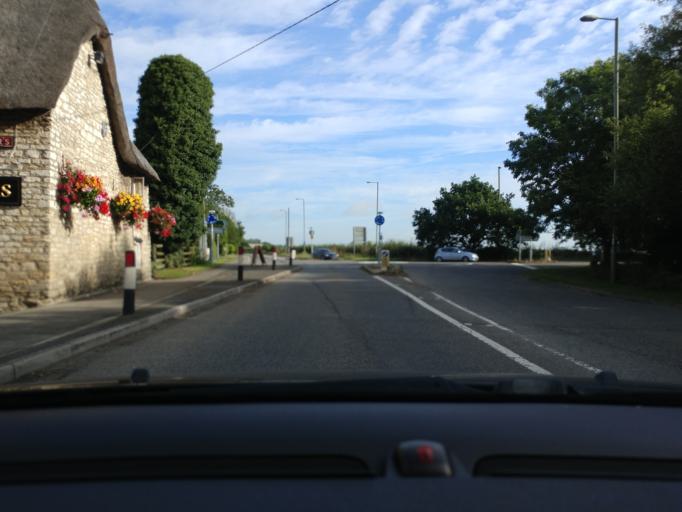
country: GB
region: England
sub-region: Oxfordshire
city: Kidlington
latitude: 51.8571
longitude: -1.2218
